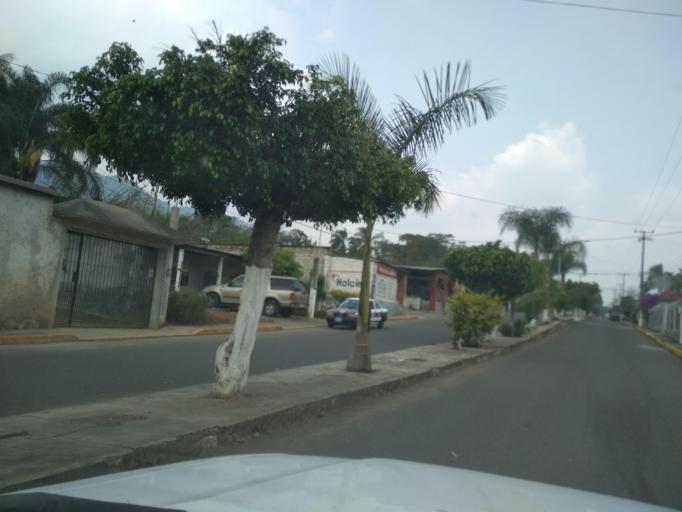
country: MX
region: Veracruz
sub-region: Cordoba
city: San Jose de Tapia
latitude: 18.8524
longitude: -96.9818
